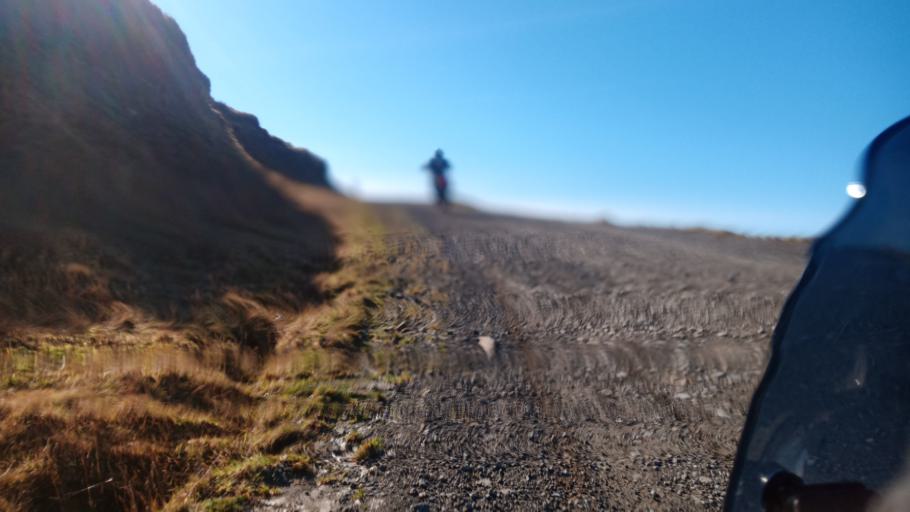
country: NZ
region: Gisborne
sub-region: Gisborne District
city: Gisborne
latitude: -38.1801
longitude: 177.8243
